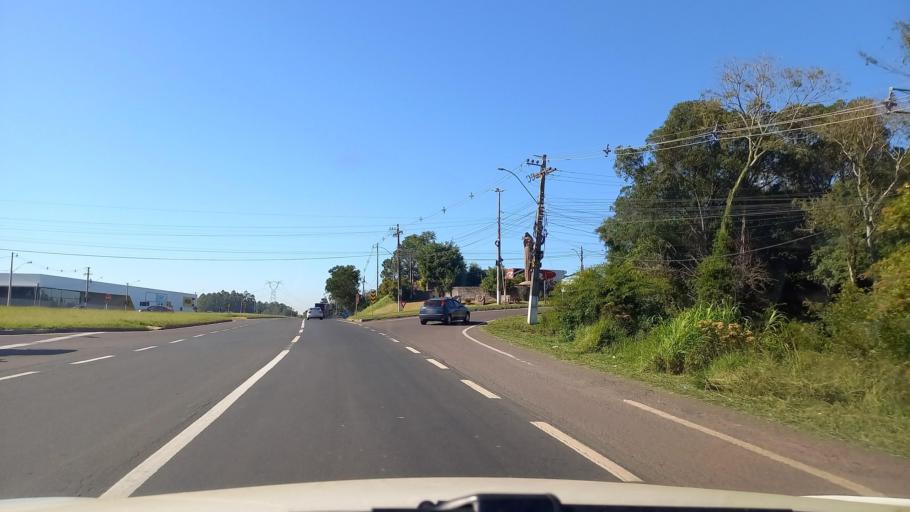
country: BR
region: Rio Grande do Sul
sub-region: Esteio
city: Esteio
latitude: -29.8479
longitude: -51.2715
